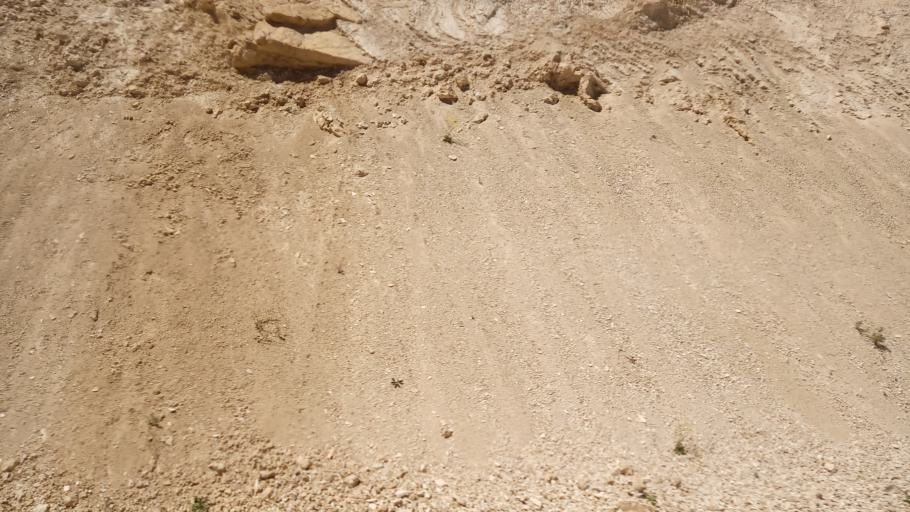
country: TR
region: Malatya
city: Darende
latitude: 38.6373
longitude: 37.4501
